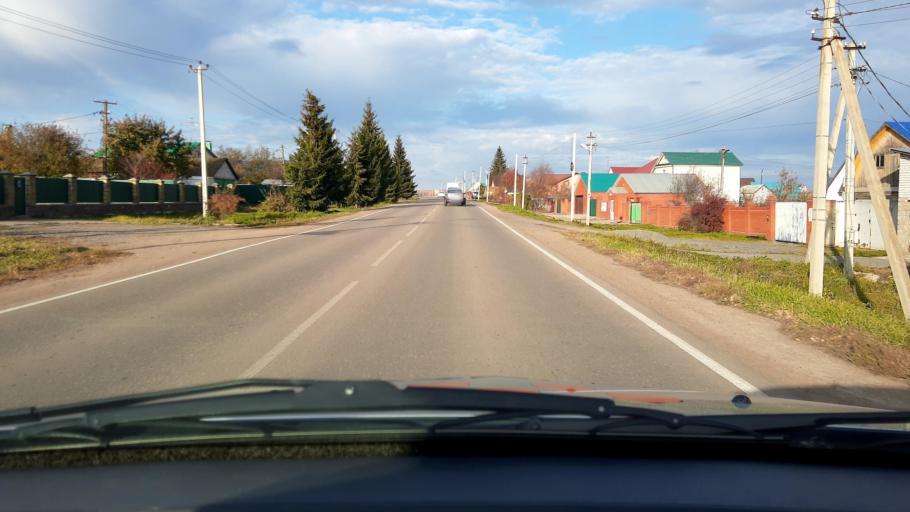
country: RU
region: Bashkortostan
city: Mikhaylovka
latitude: 54.8162
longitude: 55.7947
